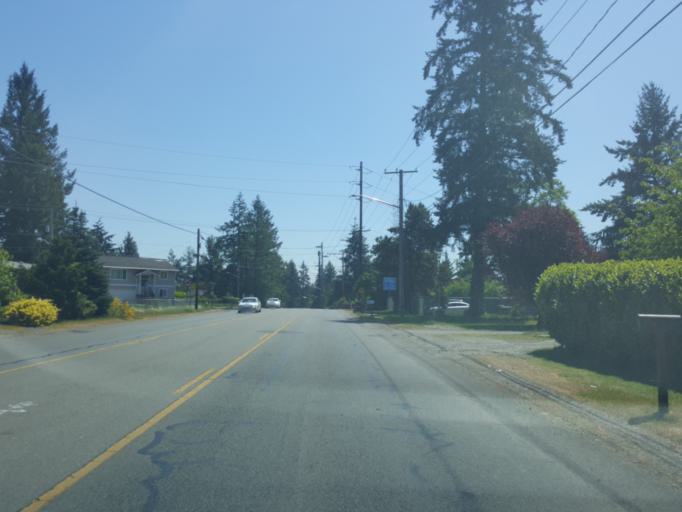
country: US
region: Washington
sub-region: Pierce County
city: Steilacoom
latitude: 47.1513
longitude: -122.5699
